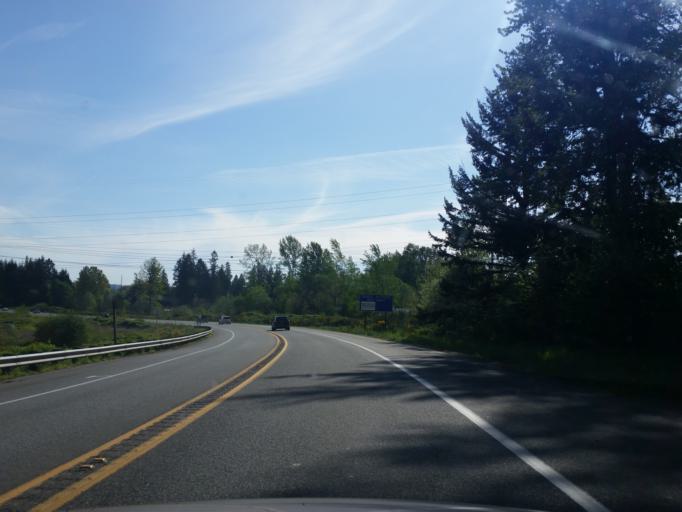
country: US
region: Washington
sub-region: Snohomish County
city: Snohomish
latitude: 47.9309
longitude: -122.1057
